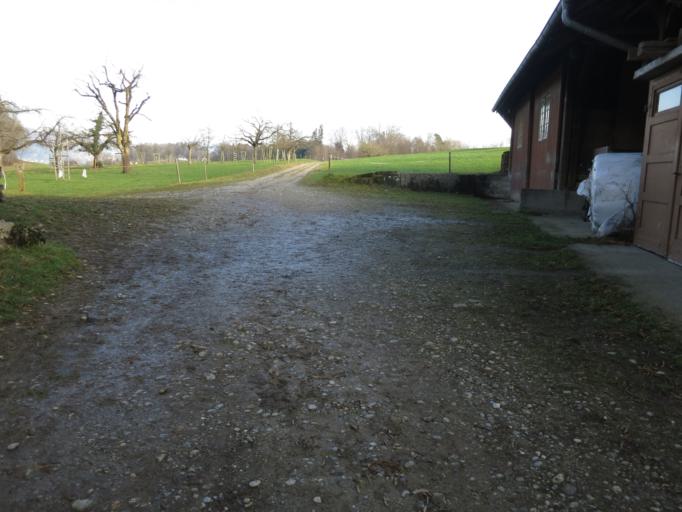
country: CH
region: Zurich
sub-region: Bezirk Hinwil
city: Wolfhausen
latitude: 47.2469
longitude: 8.8053
